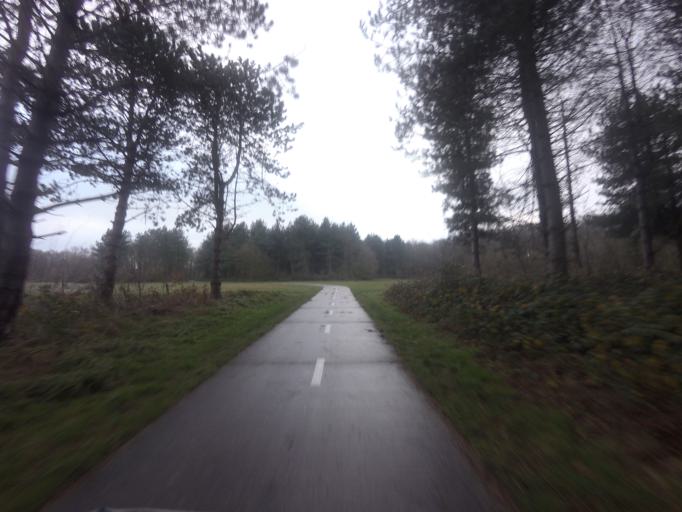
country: NL
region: North Holland
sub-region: Gemeente Texel
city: Den Burg
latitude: 53.1529
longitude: 4.8634
